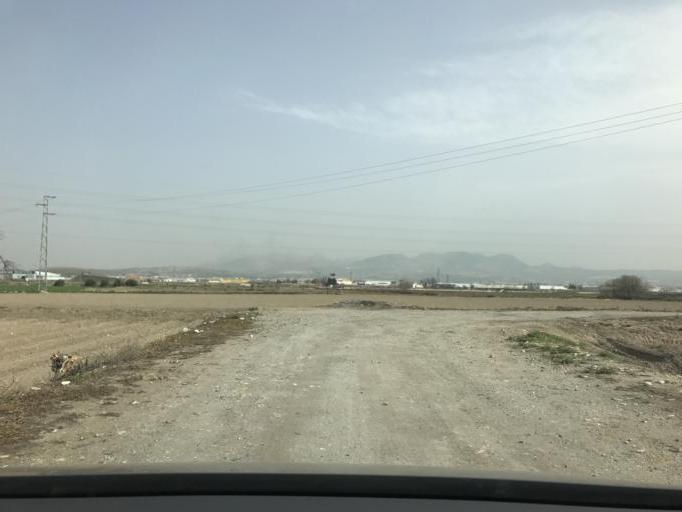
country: ES
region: Andalusia
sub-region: Provincia de Granada
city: Atarfe
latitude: 37.1996
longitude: -3.6779
